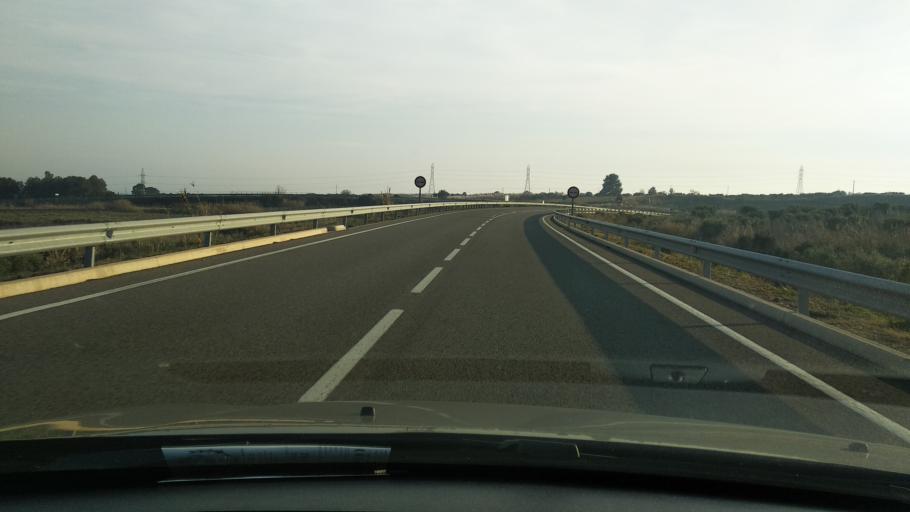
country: ES
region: Catalonia
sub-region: Provincia de Tarragona
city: les Borges del Camp
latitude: 41.1666
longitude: 1.0099
